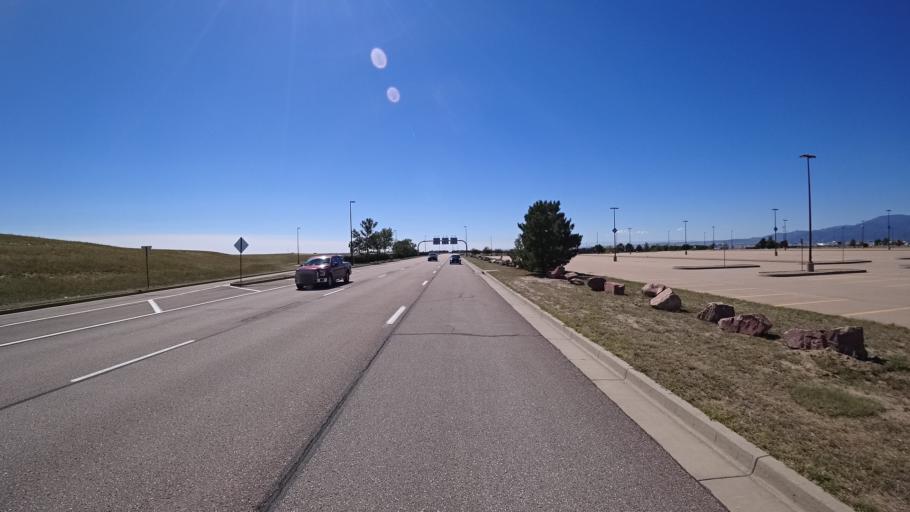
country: US
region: Colorado
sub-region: El Paso County
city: Security-Widefield
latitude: 38.7939
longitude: -104.6975
